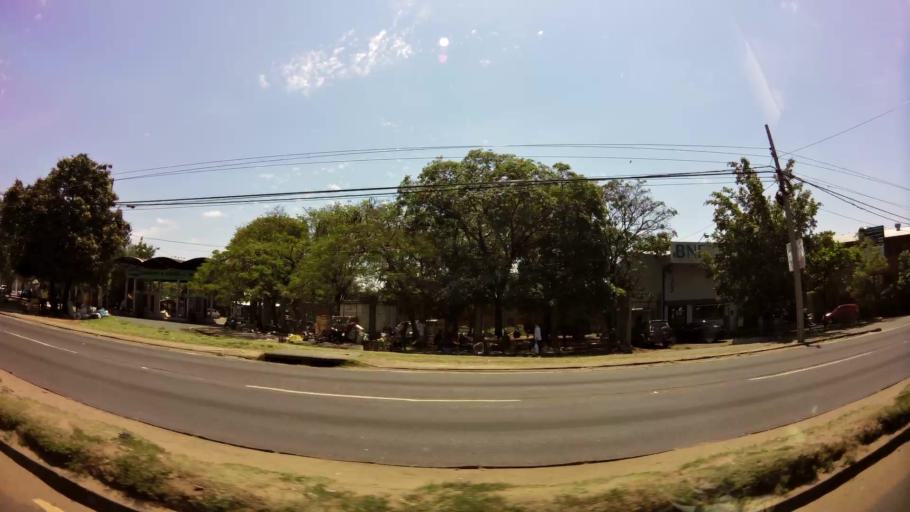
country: PY
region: Central
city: Lambare
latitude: -25.3288
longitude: -57.5715
